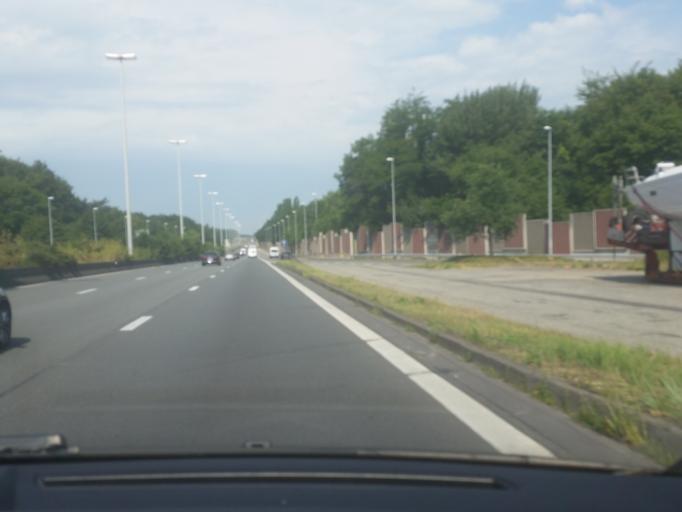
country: BE
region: Flanders
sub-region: Provincie West-Vlaanderen
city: Oostkamp
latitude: 51.1634
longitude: 3.1907
